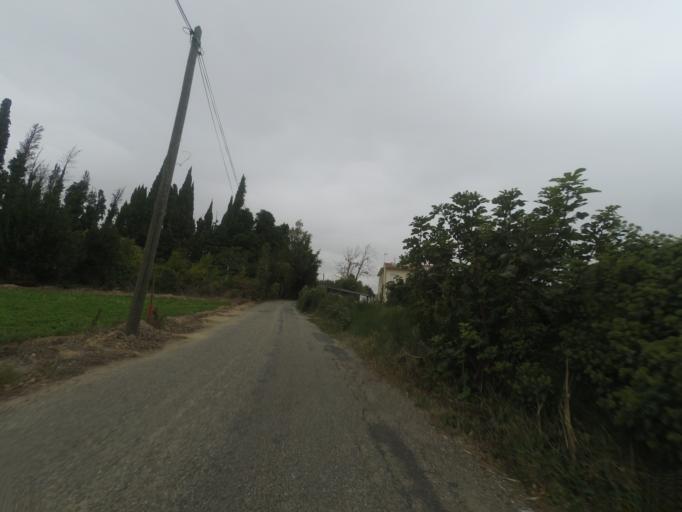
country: FR
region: Languedoc-Roussillon
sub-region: Departement des Pyrenees-Orientales
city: Saint-Esteve
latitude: 42.7028
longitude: 2.8430
